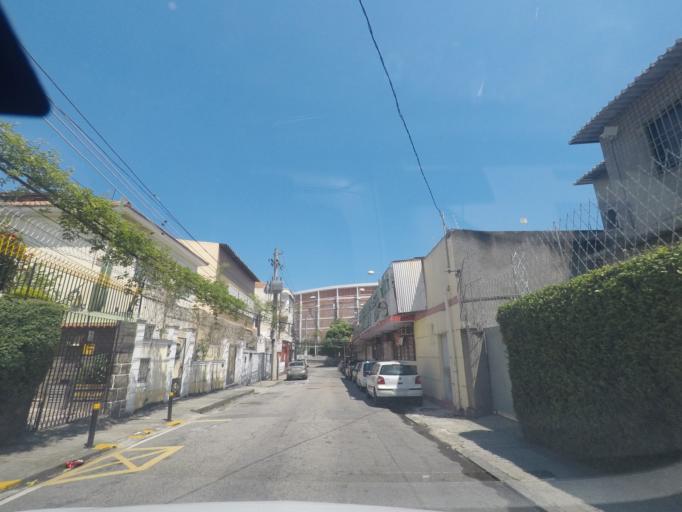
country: BR
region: Rio de Janeiro
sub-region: Rio De Janeiro
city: Rio de Janeiro
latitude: -22.8960
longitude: -43.2218
